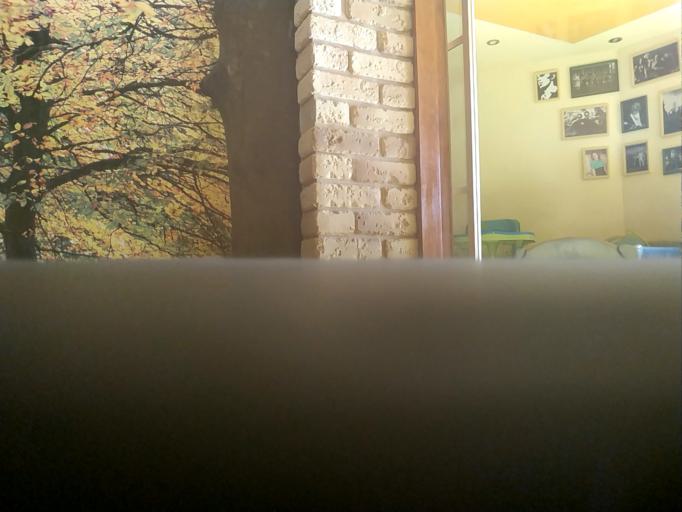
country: RU
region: Smolensk
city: Temkino
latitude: 55.0717
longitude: 34.9104
